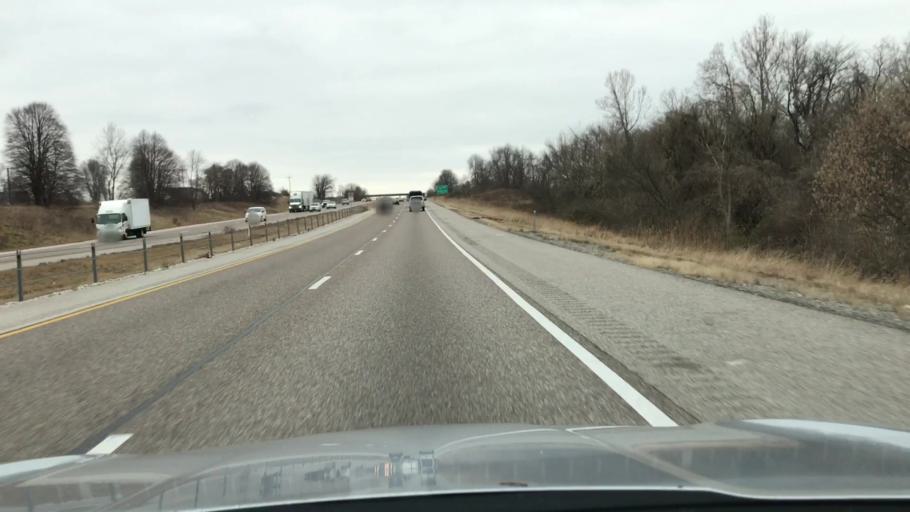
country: US
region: Illinois
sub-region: Madison County
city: Troy
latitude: 38.7656
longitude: -89.9036
